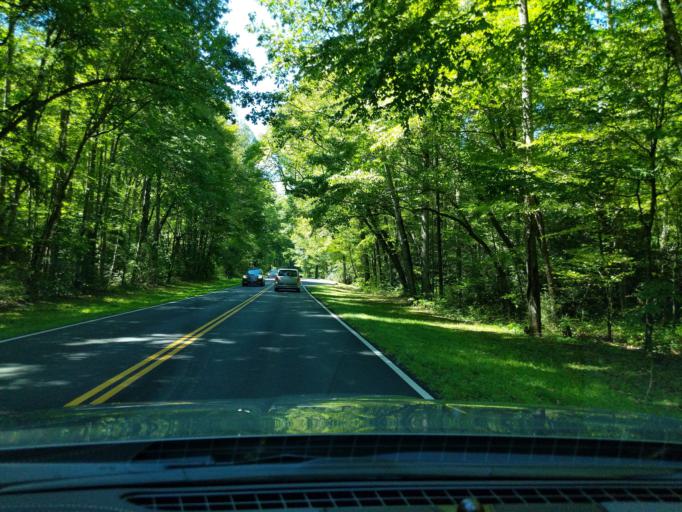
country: US
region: North Carolina
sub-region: Swain County
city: Cherokee
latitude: 35.5566
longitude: -83.3183
